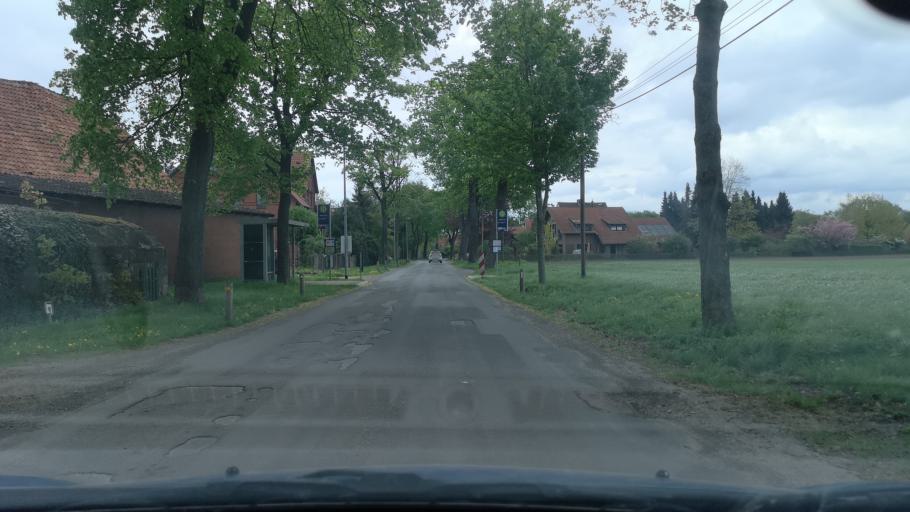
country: DE
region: Lower Saxony
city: Langenhagen
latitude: 52.4892
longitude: 9.7413
